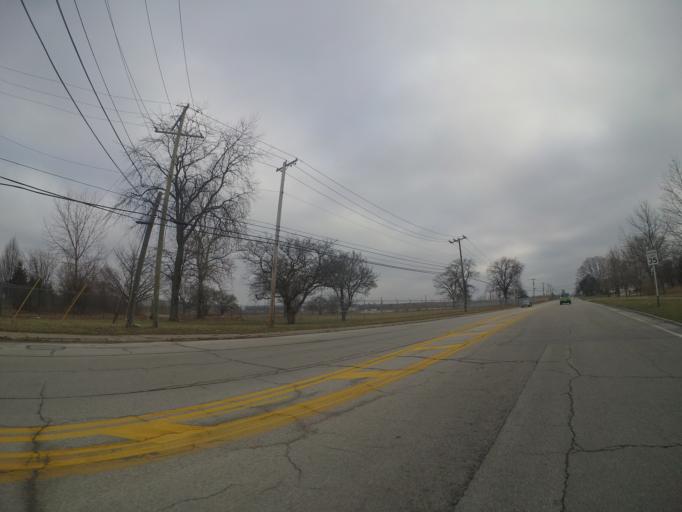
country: US
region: Ohio
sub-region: Wood County
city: Walbridge
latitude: 41.6181
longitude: -83.5128
